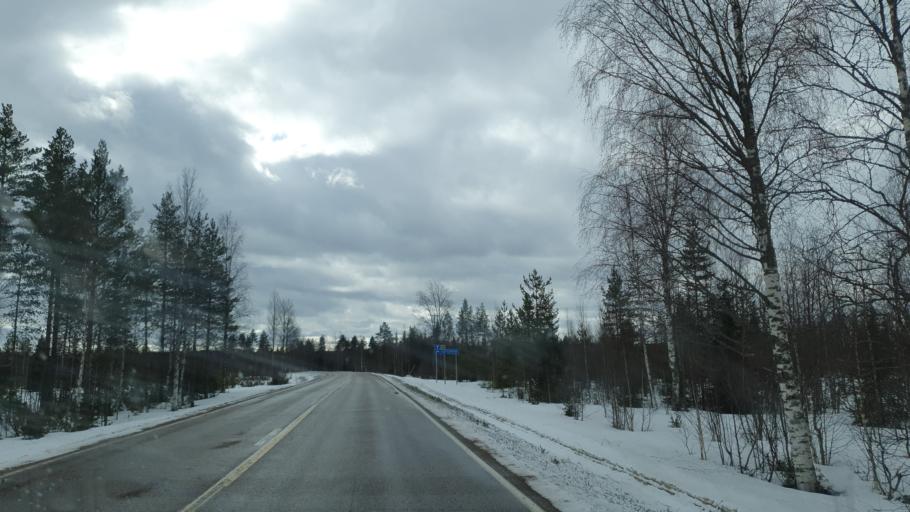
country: FI
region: Kainuu
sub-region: Kehys-Kainuu
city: Puolanka
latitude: 65.0374
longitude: 27.7035
